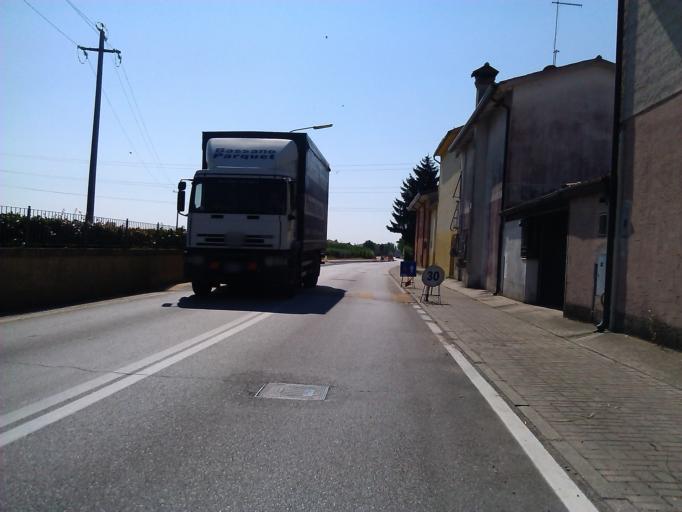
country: IT
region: Veneto
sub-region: Provincia di Vicenza
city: San Zeno-San Giuseppe
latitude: 45.7565
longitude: 11.7776
